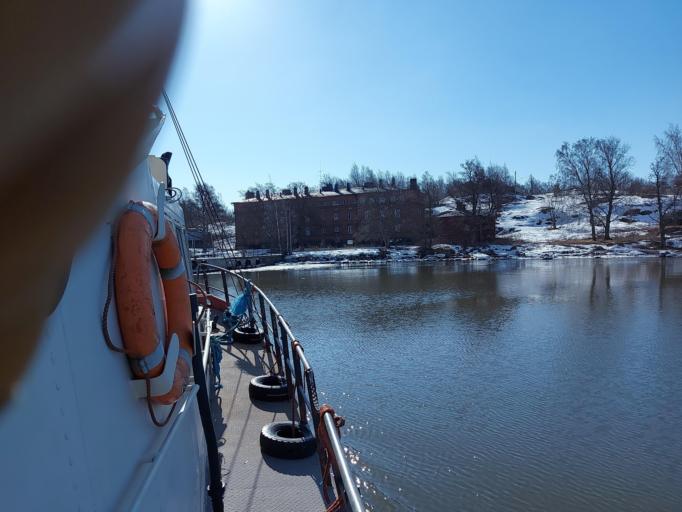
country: FI
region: Uusimaa
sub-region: Helsinki
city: Helsinki
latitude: 60.1411
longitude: 25.0064
